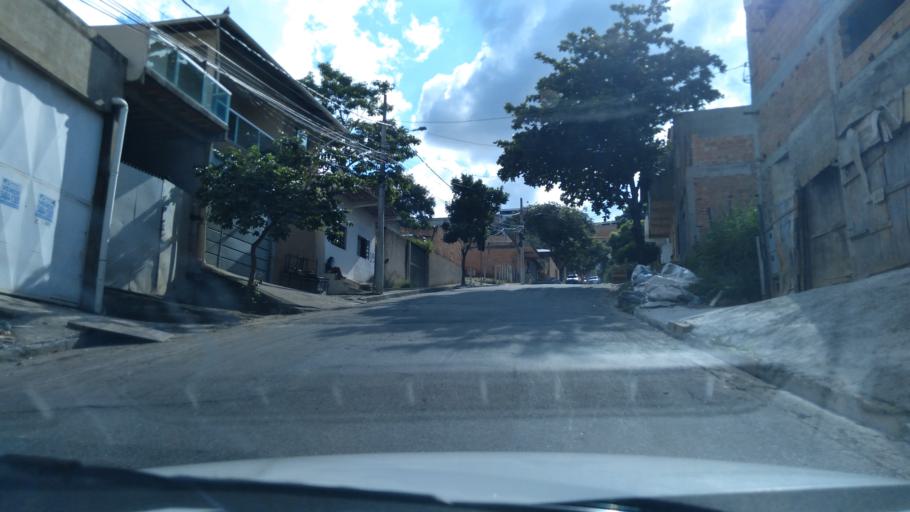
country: BR
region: Minas Gerais
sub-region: Belo Horizonte
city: Belo Horizonte
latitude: -19.8596
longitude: -43.8738
